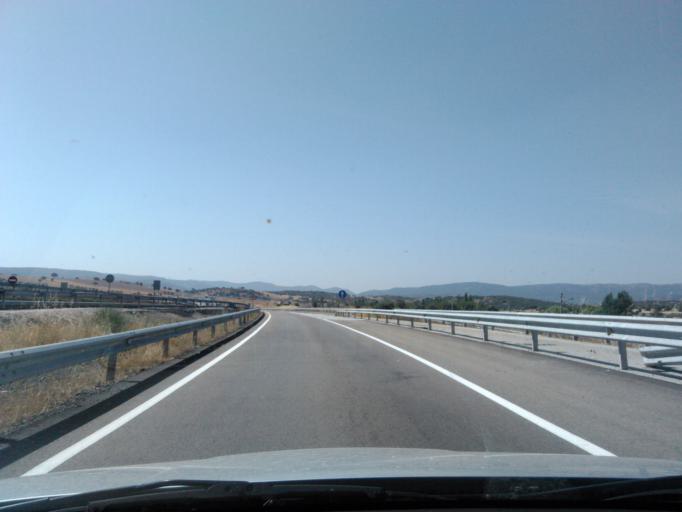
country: ES
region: Castille-La Mancha
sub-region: Provincia de Ciudad Real
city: Viso del Marques
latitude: 38.4965
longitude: -3.5040
